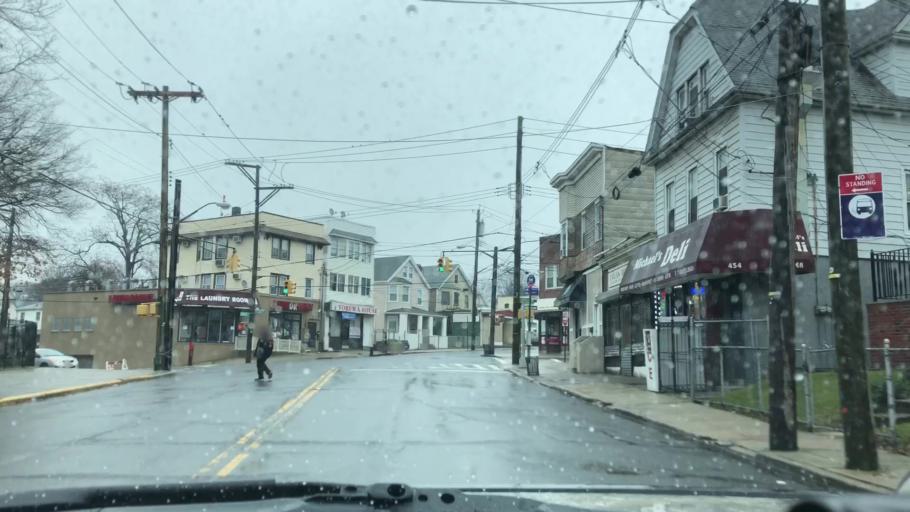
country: US
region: New Jersey
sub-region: Hudson County
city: Bayonne
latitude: 40.6340
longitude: -74.0978
